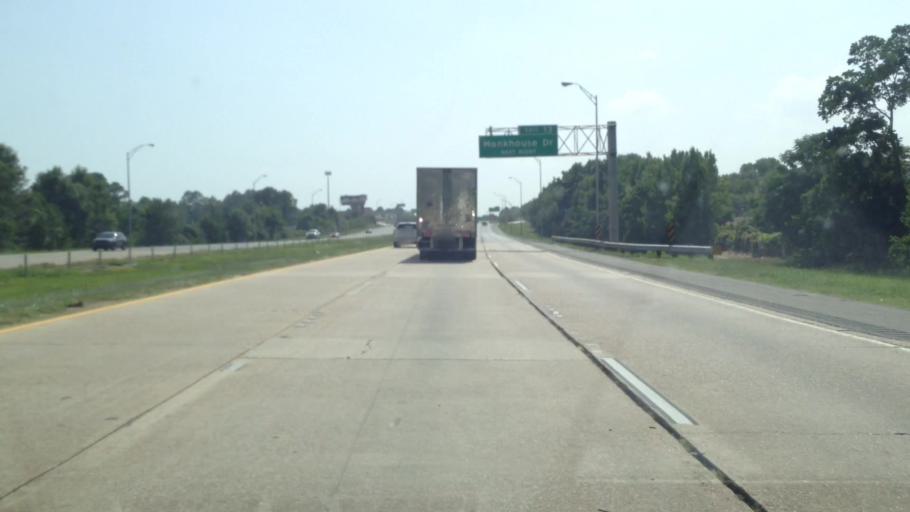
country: US
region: Louisiana
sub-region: Caddo Parish
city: Shreveport
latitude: 32.4643
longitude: -93.8195
